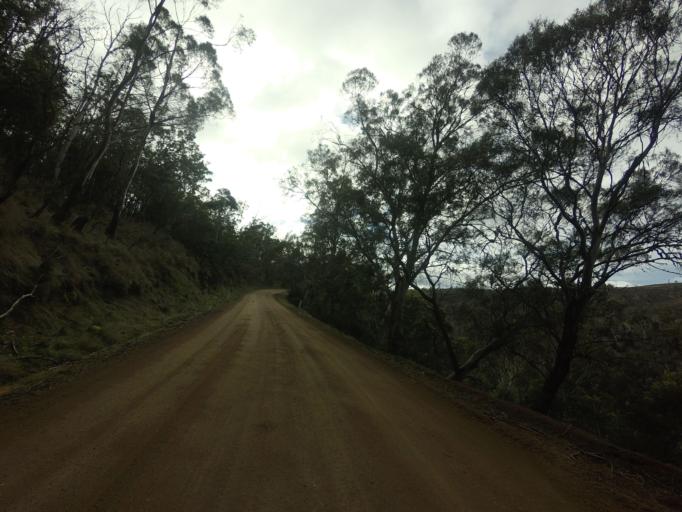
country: AU
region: Tasmania
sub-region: Derwent Valley
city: New Norfolk
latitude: -42.7404
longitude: 146.8687
